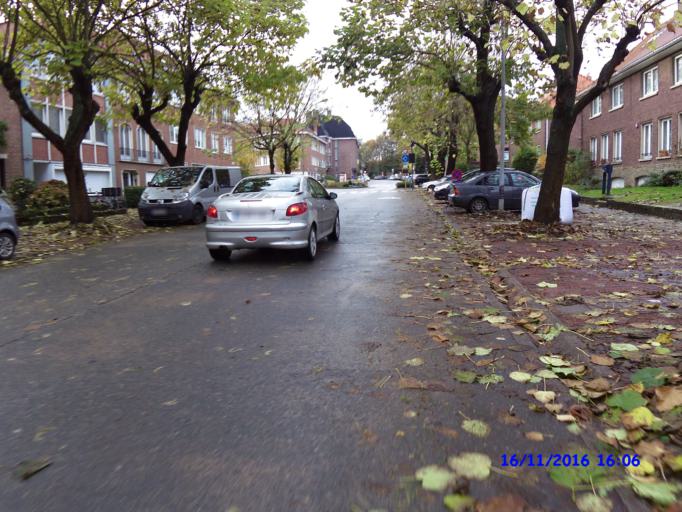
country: BE
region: Flanders
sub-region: Provincie Vlaams-Brabant
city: Diegem
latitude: 50.8506
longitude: 4.4129
